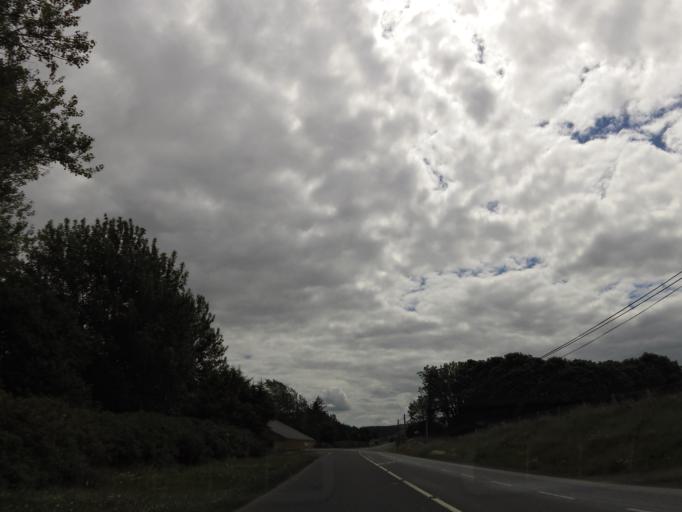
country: IE
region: Munster
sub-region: North Tipperary
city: Templemore
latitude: 52.7679
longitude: -8.0226
